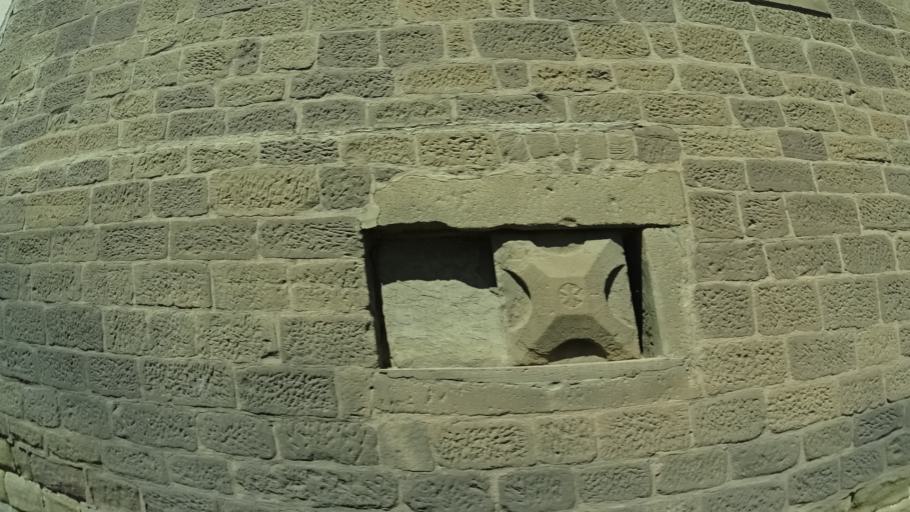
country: DE
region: Bavaria
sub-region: Regierungsbezirk Unterfranken
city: Euerbach
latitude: 50.0625
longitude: 10.1304
